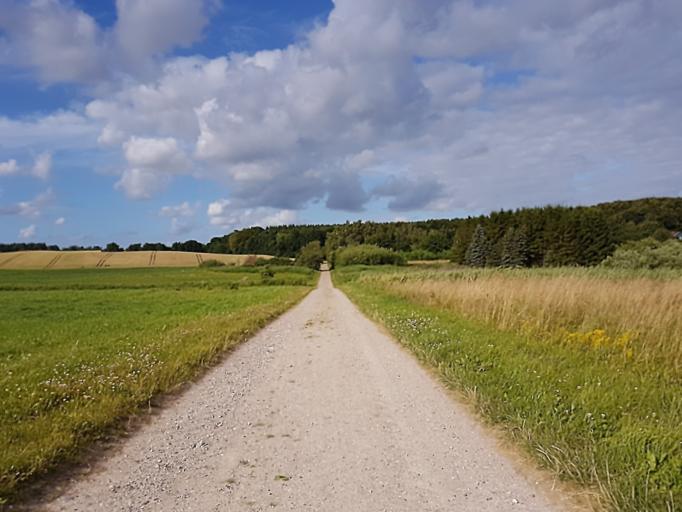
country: DK
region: Capital Region
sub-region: Egedal Kommune
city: Ganlose
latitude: 55.7943
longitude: 12.2879
